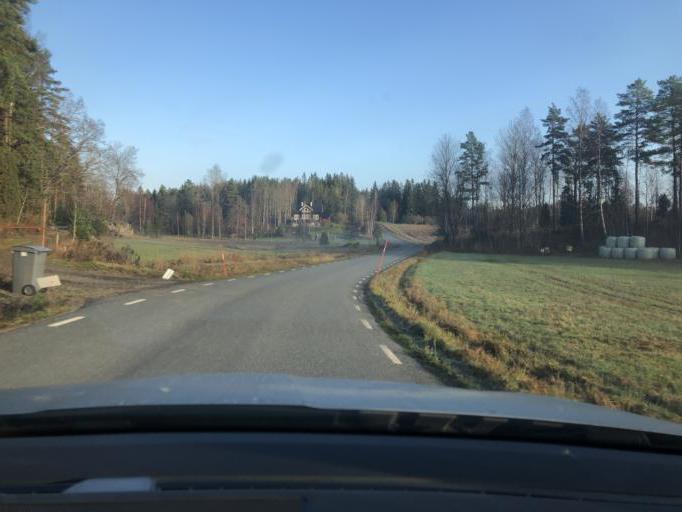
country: SE
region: Soedermanland
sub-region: Flens Kommun
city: Halleforsnas
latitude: 59.0834
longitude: 16.4224
